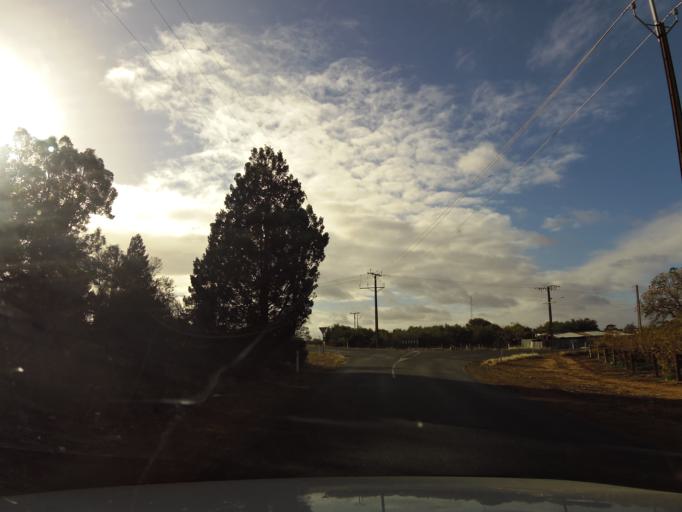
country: AU
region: South Australia
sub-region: Berri and Barmera
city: Berri
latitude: -34.2711
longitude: 140.5871
